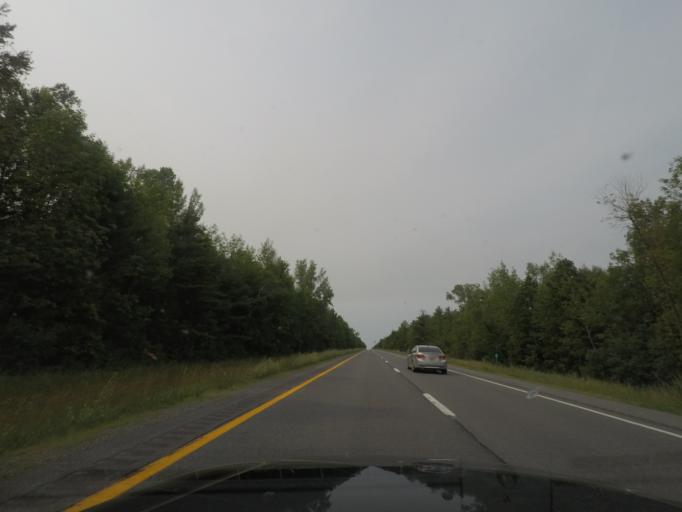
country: US
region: New York
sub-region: Clinton County
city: Champlain
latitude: 44.9547
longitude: -73.4487
